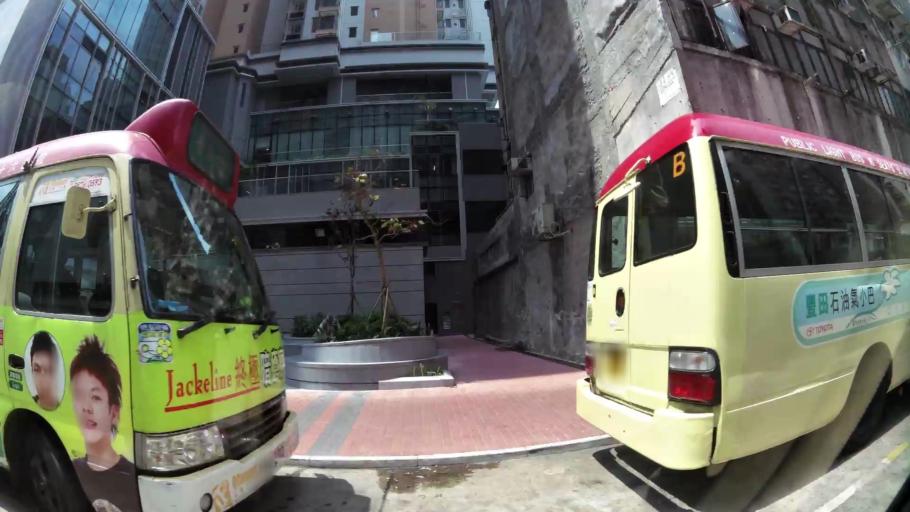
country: HK
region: Sham Shui Po
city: Sham Shui Po
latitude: 22.3391
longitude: 114.1544
